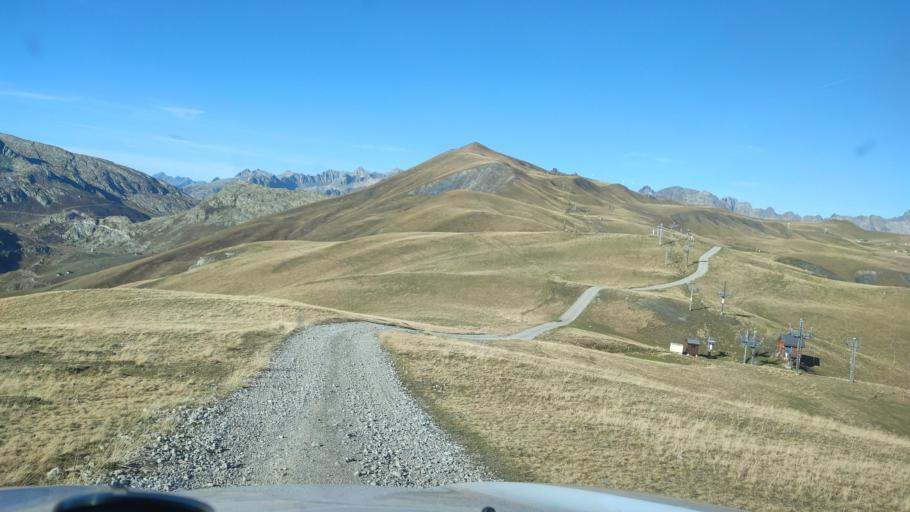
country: FR
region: Rhone-Alpes
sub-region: Departement de la Savoie
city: Saint-Jean-de-Maurienne
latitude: 45.2368
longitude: 6.2393
